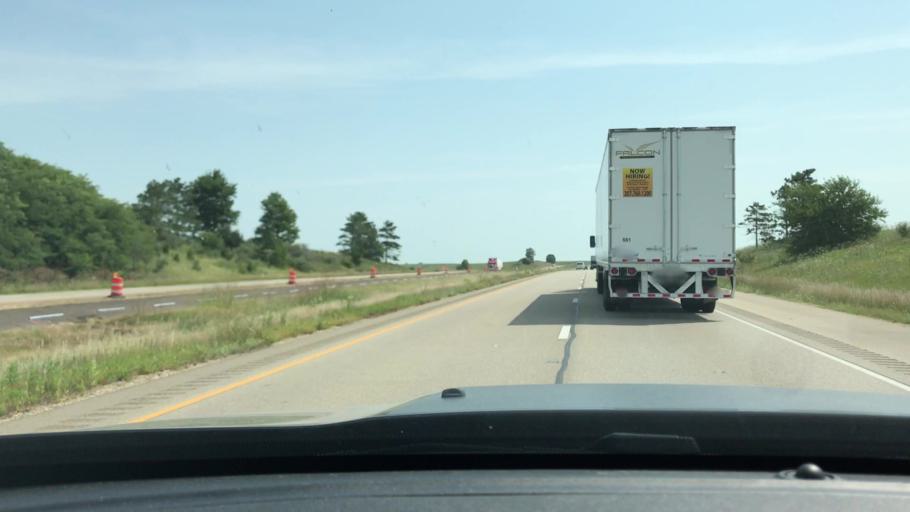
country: US
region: Illinois
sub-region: Bureau County
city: Walnut
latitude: 41.3919
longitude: -89.6525
